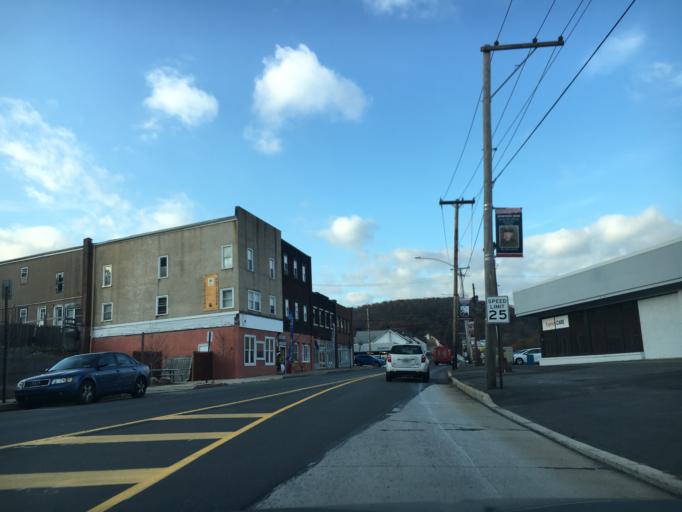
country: US
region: Pennsylvania
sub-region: Carbon County
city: Lehighton
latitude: 40.8384
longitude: -75.7093
